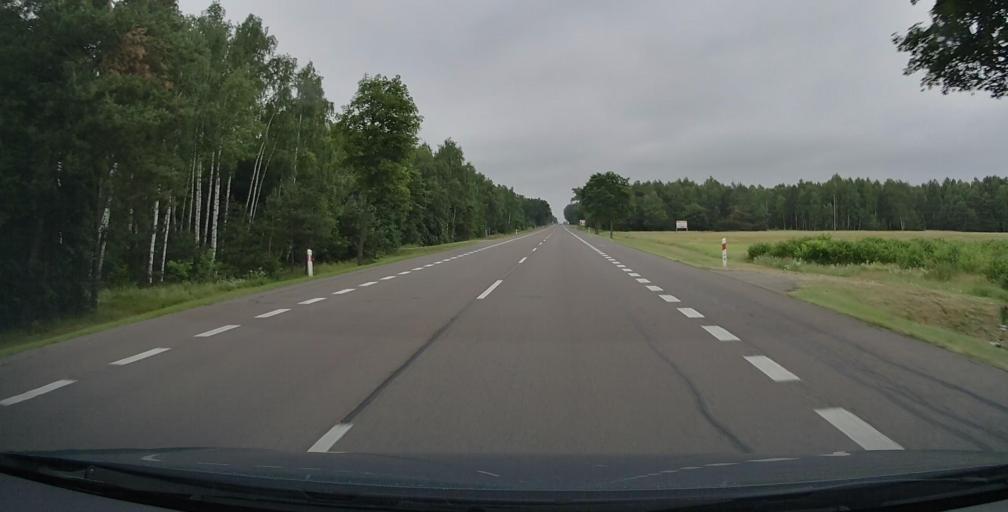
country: PL
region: Lublin Voivodeship
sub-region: Powiat bialski
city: Lesna Podlaska
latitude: 52.0367
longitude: 22.9930
